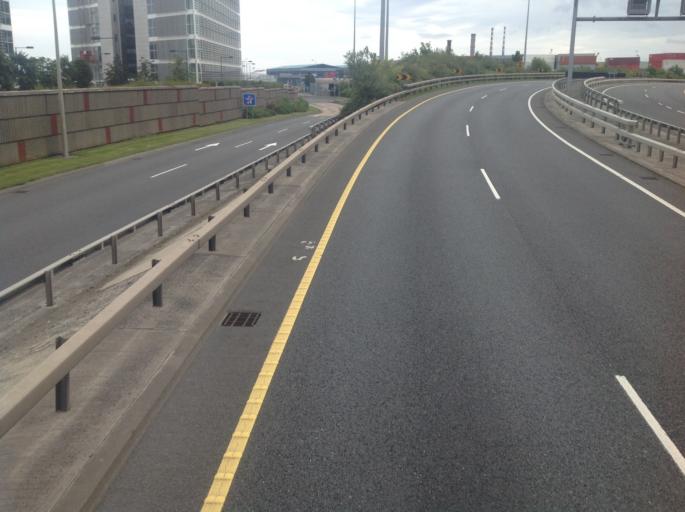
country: IE
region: Leinster
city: Ringsend
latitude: 53.3554
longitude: -6.2248
